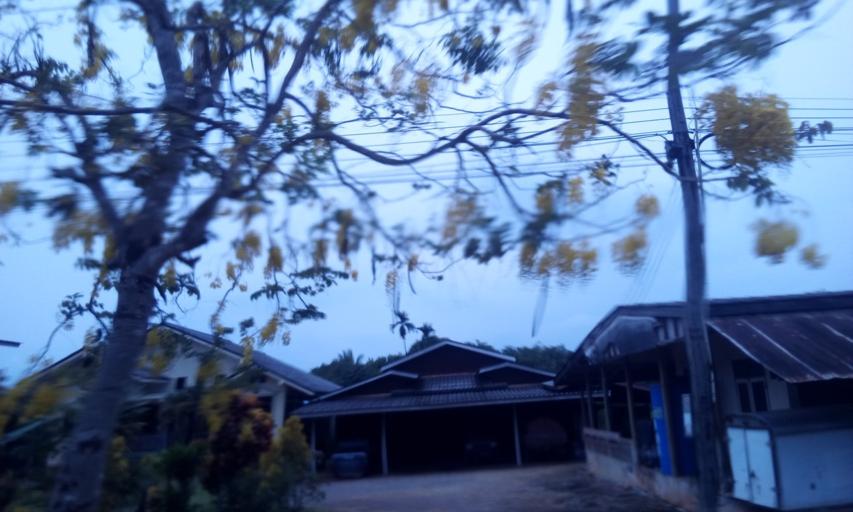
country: TH
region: Trat
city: Laem Ngop
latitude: 12.2484
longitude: 102.2932
